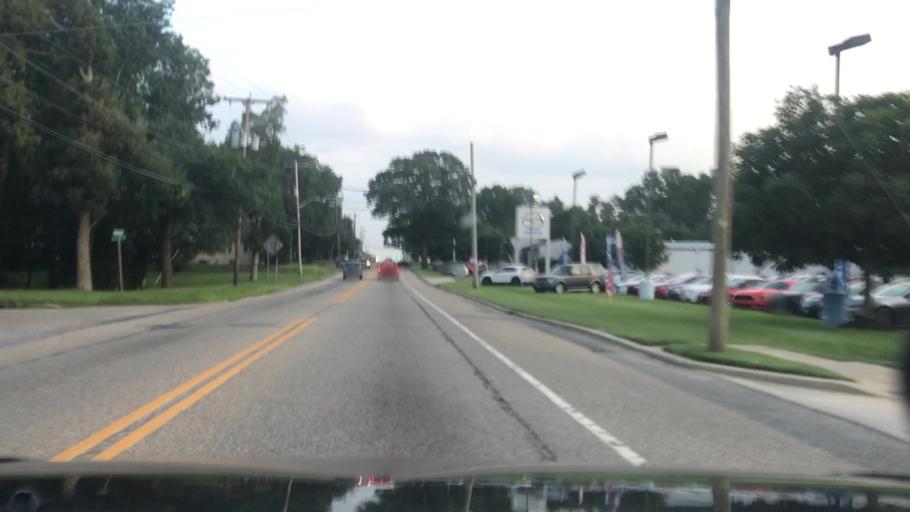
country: US
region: New Jersey
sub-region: Ocean County
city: Silver Ridge
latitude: 39.9968
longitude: -74.2119
